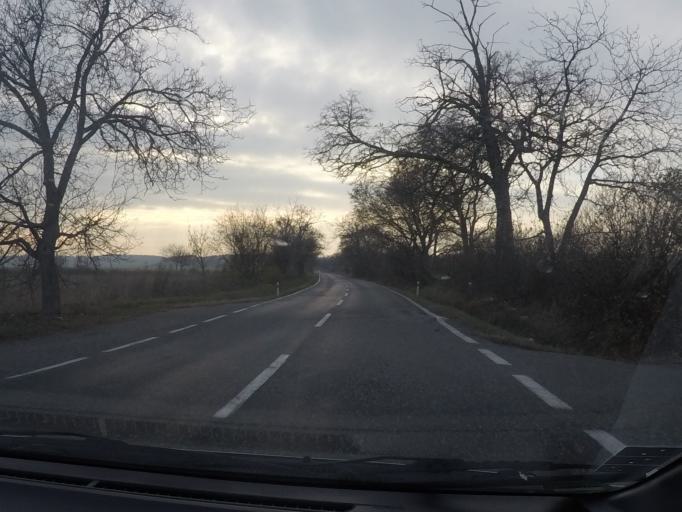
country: SK
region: Nitriansky
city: Svodin
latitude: 48.0591
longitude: 18.5026
